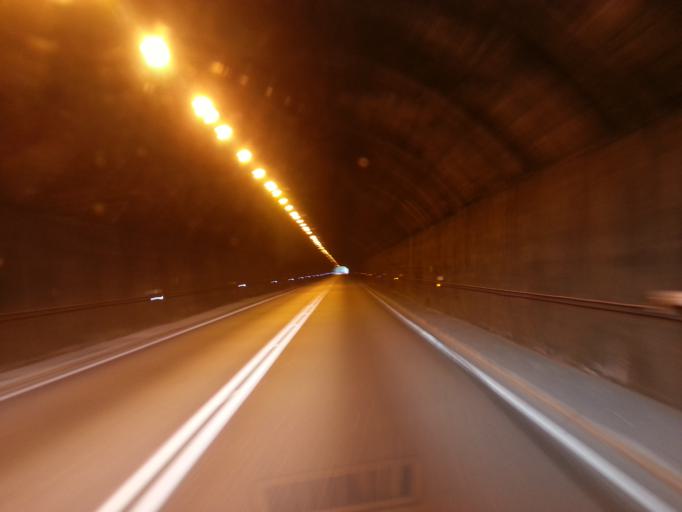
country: ES
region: Catalonia
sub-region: Provincia de Barcelona
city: Monistrol de Montserrat
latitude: 41.6273
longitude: 1.8479
